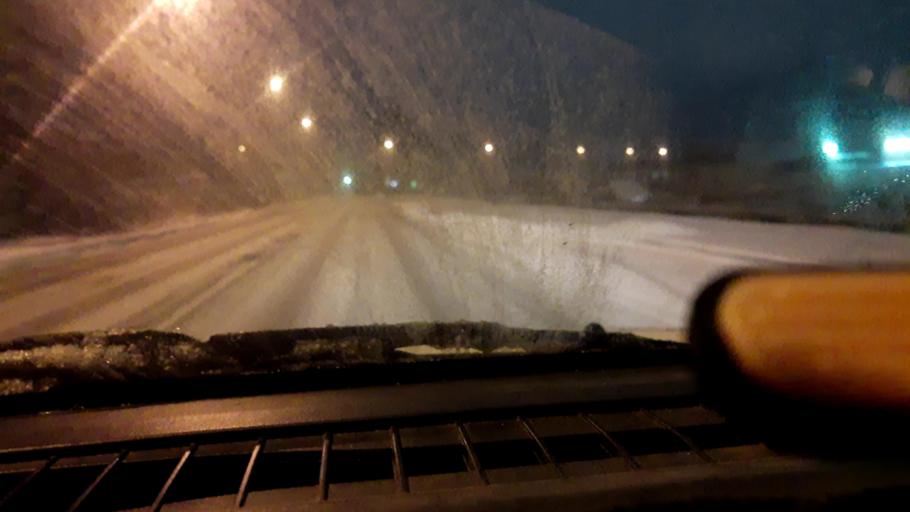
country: RU
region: Nizjnij Novgorod
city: Kstovo
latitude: 56.1402
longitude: 44.1928
